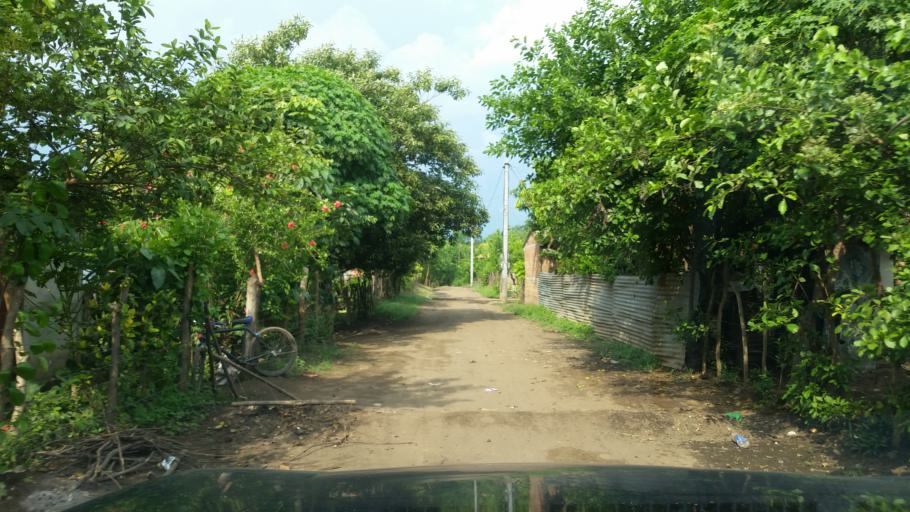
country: NI
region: Chinandega
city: Puerto Morazan
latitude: 12.7649
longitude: -87.1244
